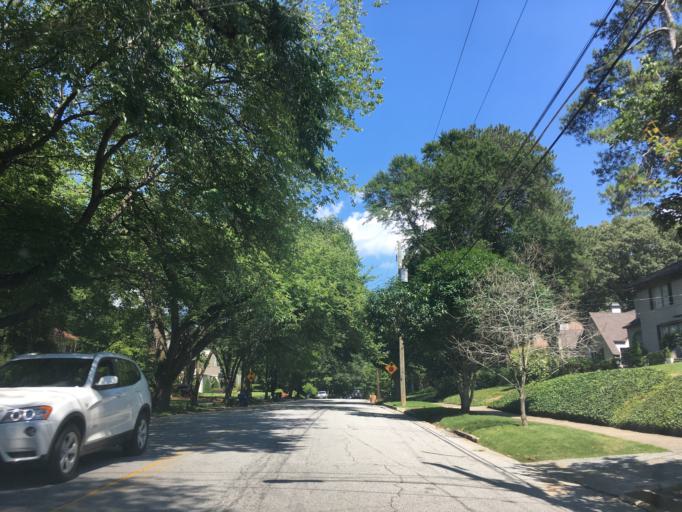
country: US
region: Georgia
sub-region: DeKalb County
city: Druid Hills
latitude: 33.7996
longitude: -84.3653
